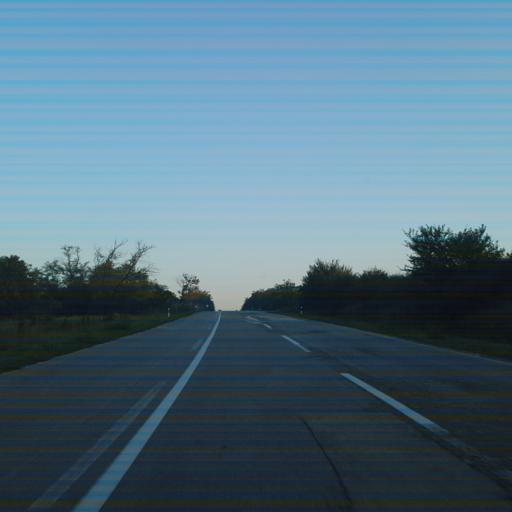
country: RS
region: Central Serbia
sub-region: Zajecarski Okrug
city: Zajecar
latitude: 43.9949
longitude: 22.3023
